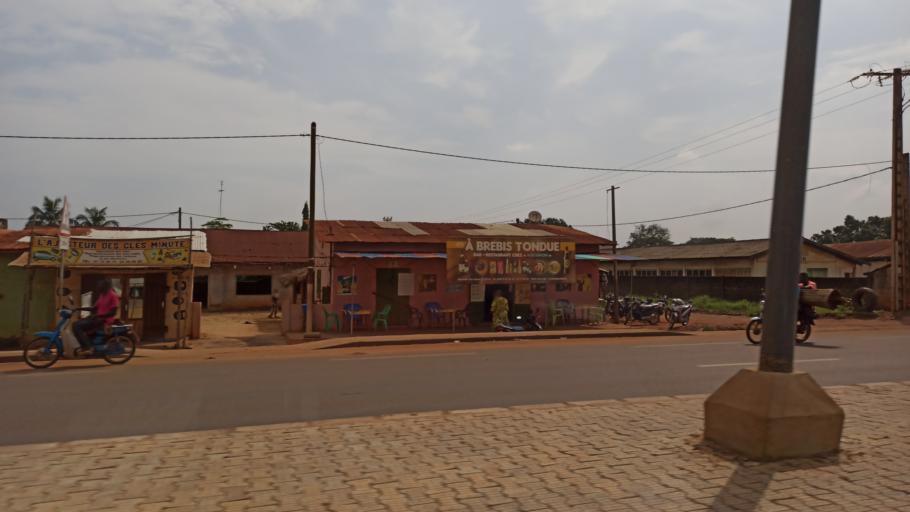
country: BJ
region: Queme
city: Porto-Novo
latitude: 6.5179
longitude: 2.6036
